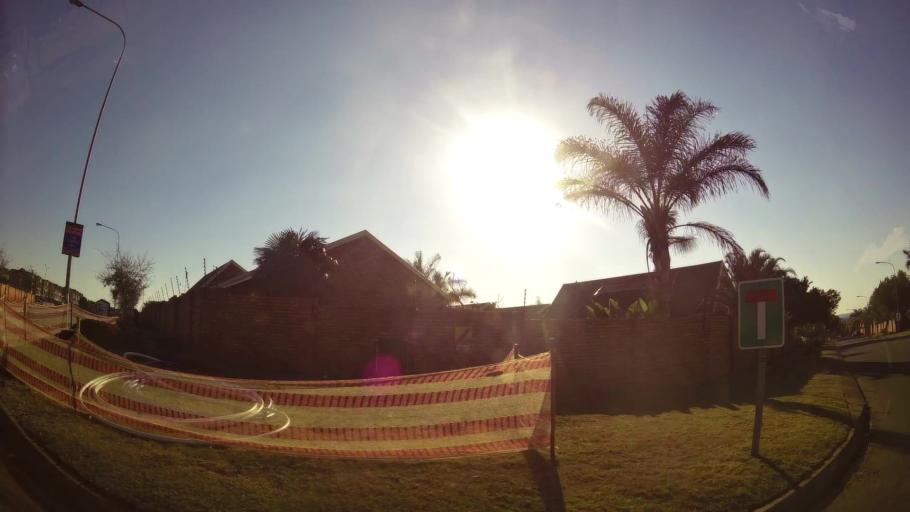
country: ZA
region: Gauteng
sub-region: City of Tshwane Metropolitan Municipality
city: Centurion
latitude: -25.8804
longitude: 28.1424
